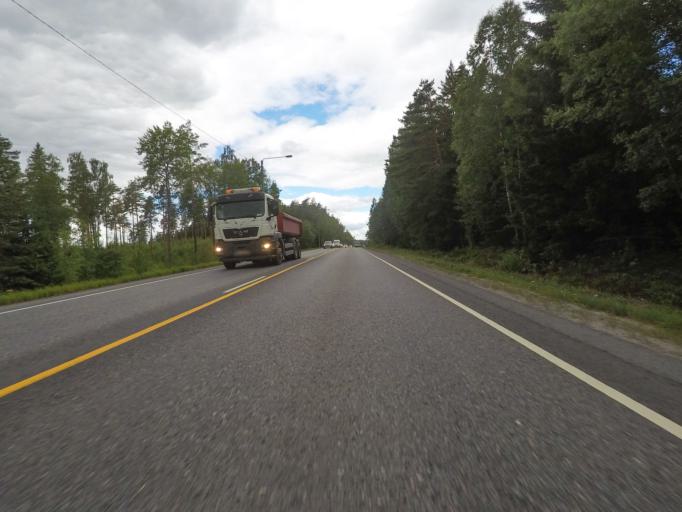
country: FI
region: Varsinais-Suomi
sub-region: Turku
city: Piikkioe
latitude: 60.4464
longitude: 22.4732
